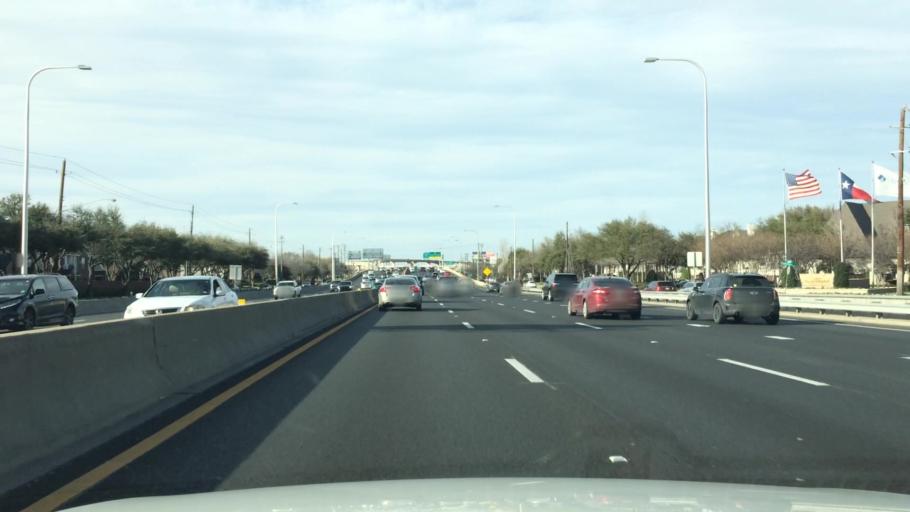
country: US
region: Texas
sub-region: Dallas County
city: Addison
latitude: 33.0032
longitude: -96.8291
